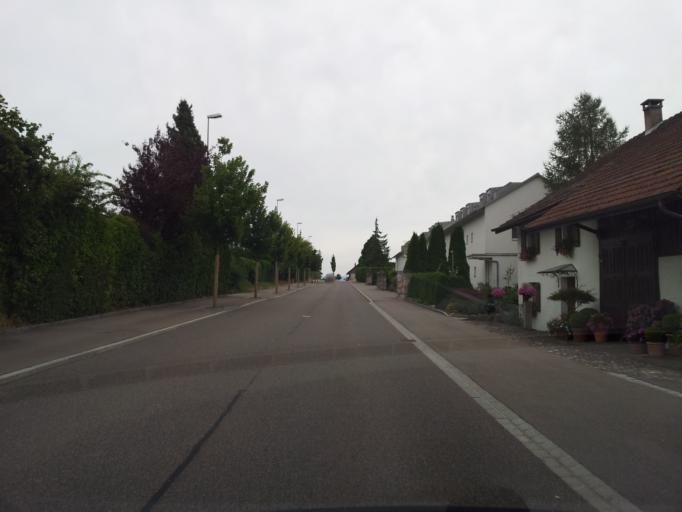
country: CH
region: Aargau
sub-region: Bezirk Bremgarten
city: Berikon
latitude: 47.3467
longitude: 8.3777
